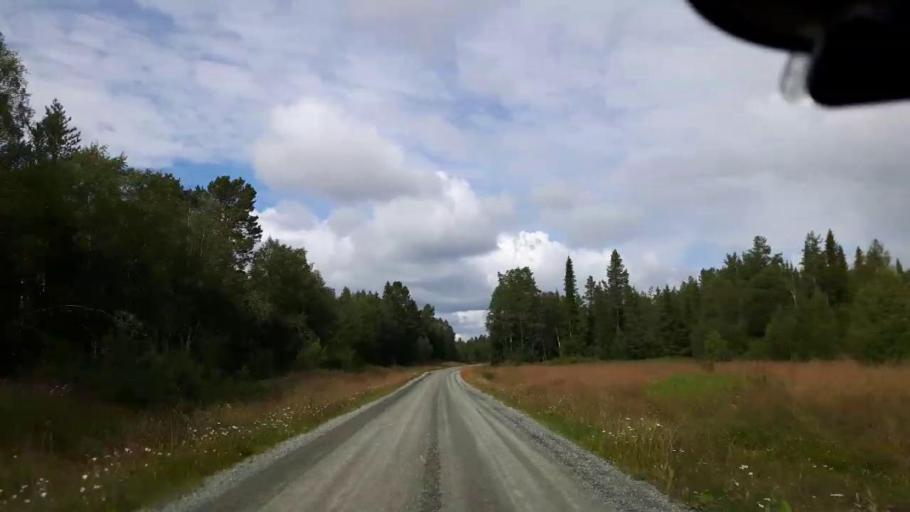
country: SE
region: Jaemtland
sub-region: Krokoms Kommun
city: Valla
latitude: 63.5435
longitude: 13.9178
